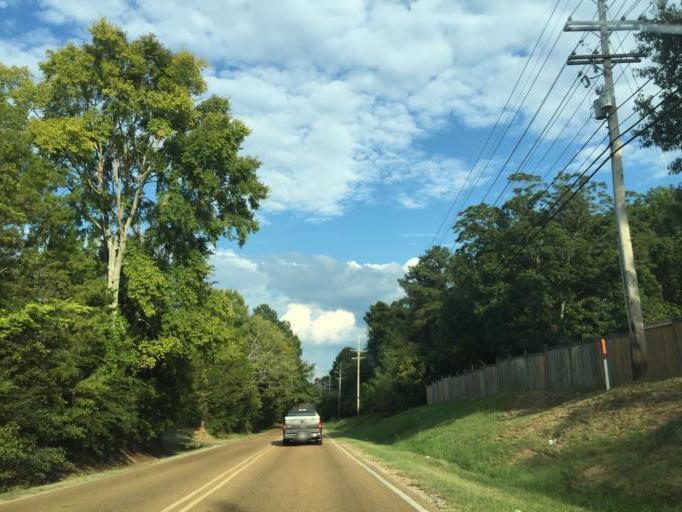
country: US
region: Mississippi
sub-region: Madison County
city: Madison
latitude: 32.4650
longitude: -90.0854
